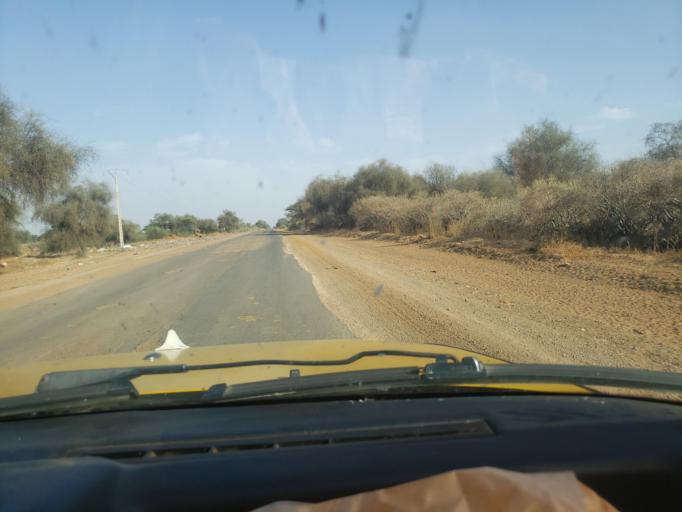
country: SN
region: Louga
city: Louga
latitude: 15.5096
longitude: -15.9796
